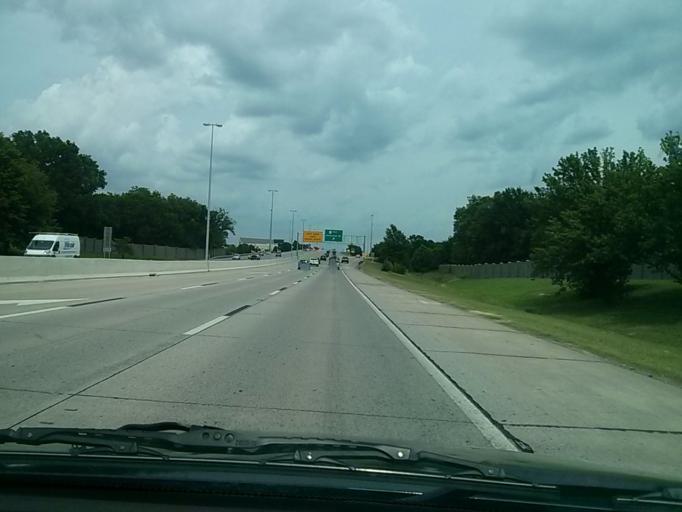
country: US
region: Oklahoma
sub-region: Tulsa County
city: Jenks
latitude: 36.0251
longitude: -95.8941
